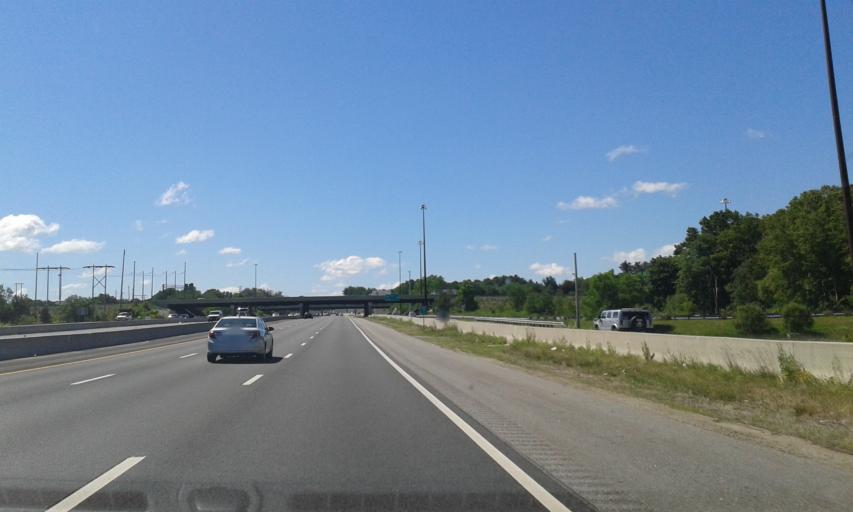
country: US
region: Massachusetts
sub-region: Middlesex County
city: Lowell
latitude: 42.6101
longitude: -71.3270
